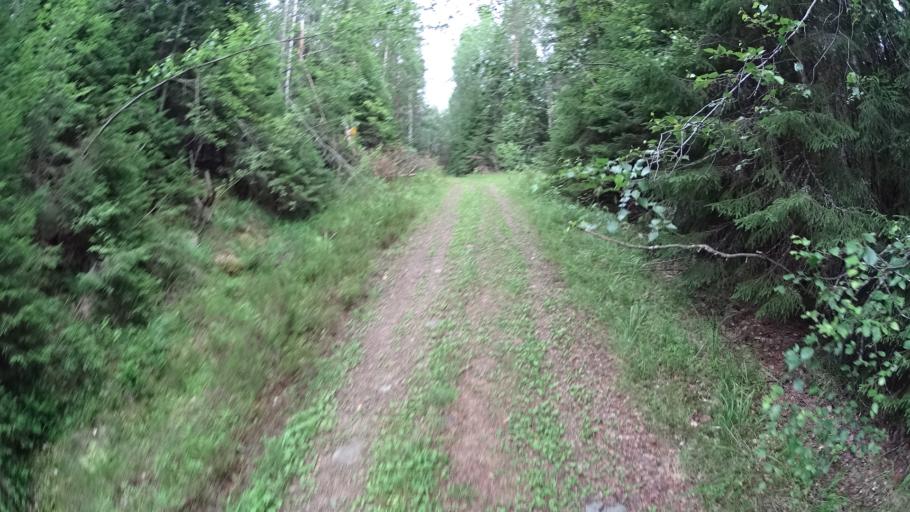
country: FI
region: Southern Savonia
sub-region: Mikkeli
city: Maentyharju
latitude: 61.1738
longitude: 26.8971
